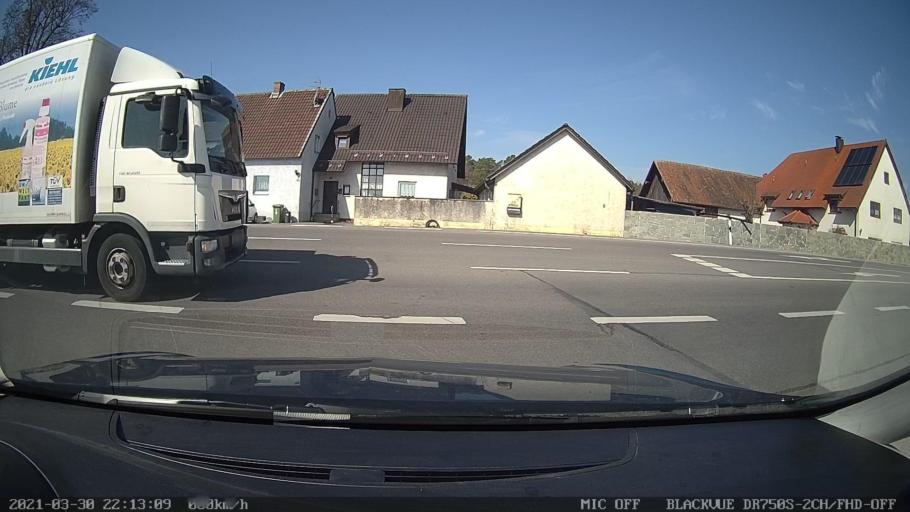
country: DE
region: Bavaria
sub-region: Upper Palatinate
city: Zeitlarn
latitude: 49.0919
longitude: 12.1208
